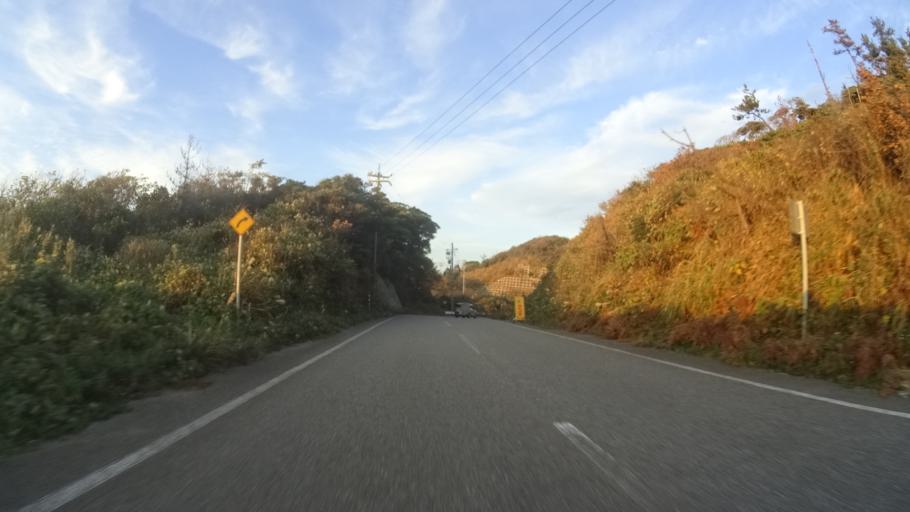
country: JP
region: Ishikawa
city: Nanao
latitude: 37.2182
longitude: 136.6965
